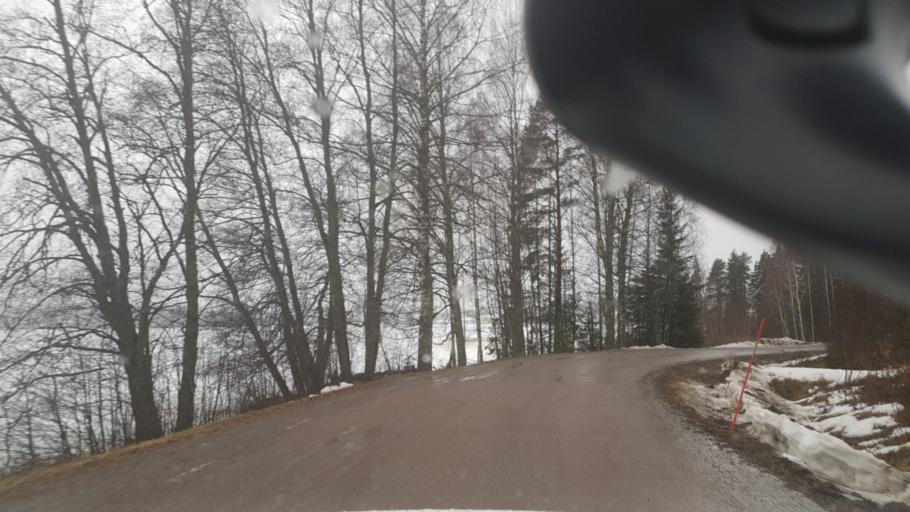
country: SE
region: Vaermland
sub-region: Eda Kommun
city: Amotfors
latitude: 59.8259
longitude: 12.3630
